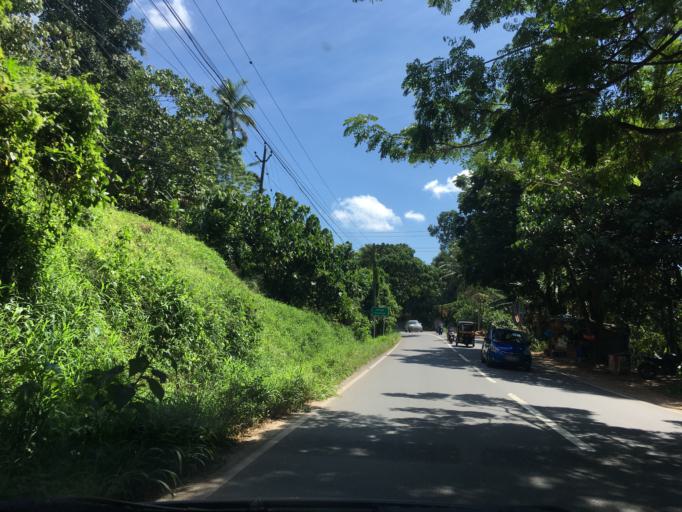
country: IN
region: Kerala
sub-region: Thiruvananthapuram
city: Nedumangad
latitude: 8.5673
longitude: 76.9848
